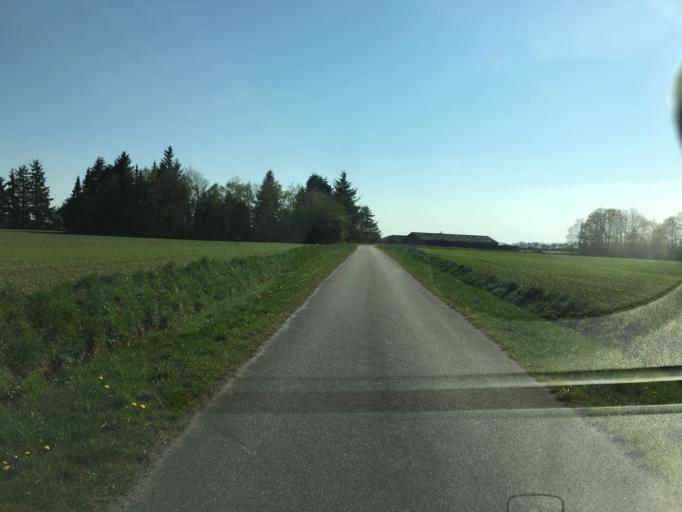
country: DK
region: South Denmark
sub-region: Tonder Kommune
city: Toftlund
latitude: 55.1882
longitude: 9.1120
